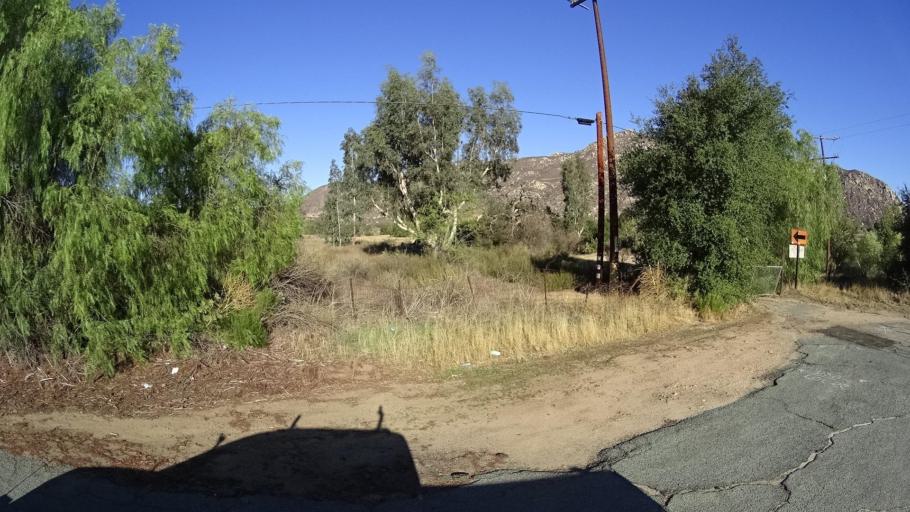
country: MX
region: Baja California
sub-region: Tecate
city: Lomas de Santa Anita
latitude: 32.6072
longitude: -116.6954
